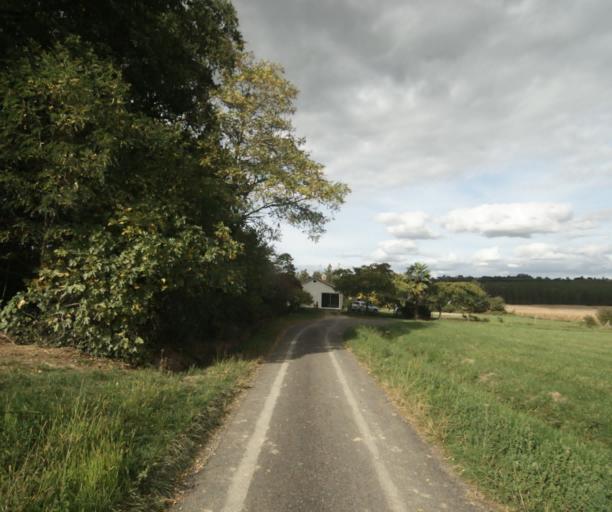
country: FR
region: Midi-Pyrenees
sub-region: Departement du Gers
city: Gondrin
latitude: 43.8524
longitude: 0.2238
